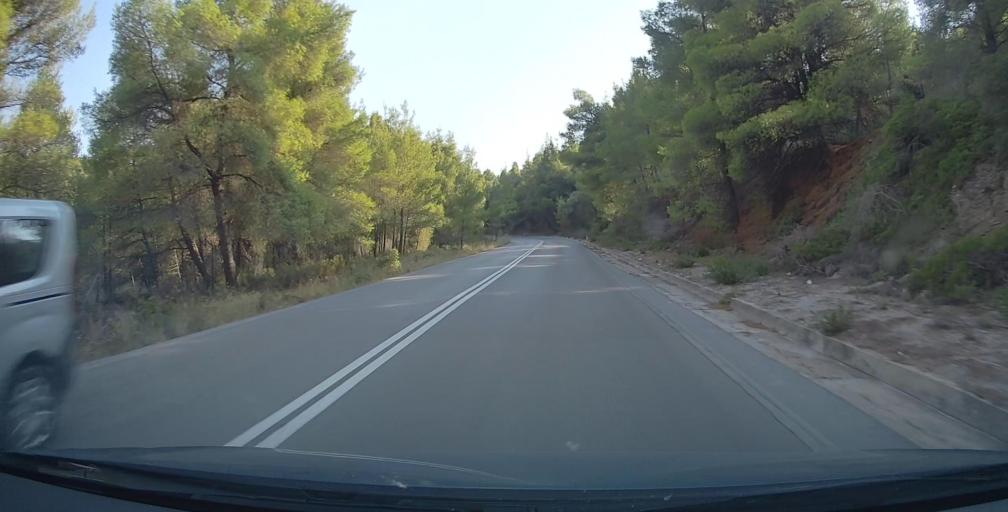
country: GR
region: Central Macedonia
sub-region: Nomos Chalkidikis
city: Neos Marmaras
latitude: 40.0669
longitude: 23.8038
